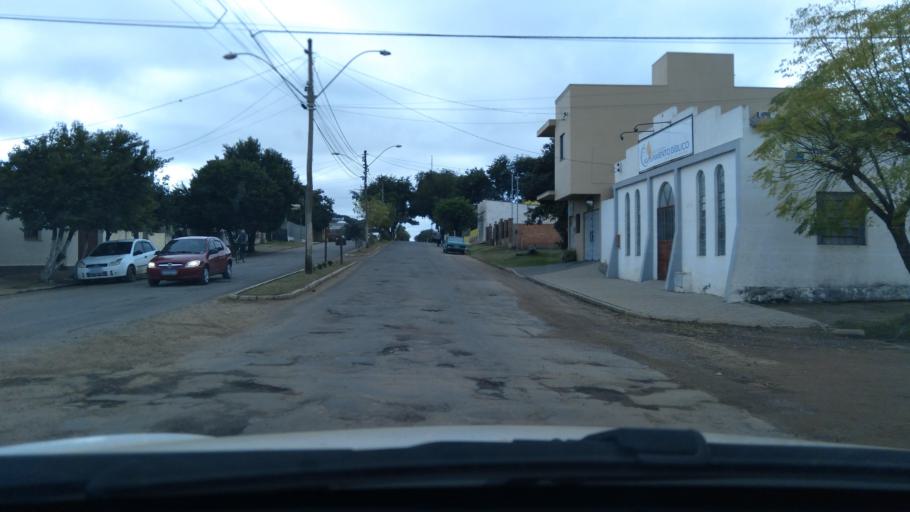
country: BR
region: Rio Grande do Sul
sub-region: Dom Pedrito
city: Dom Pedrito
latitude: -30.9710
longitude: -54.6733
